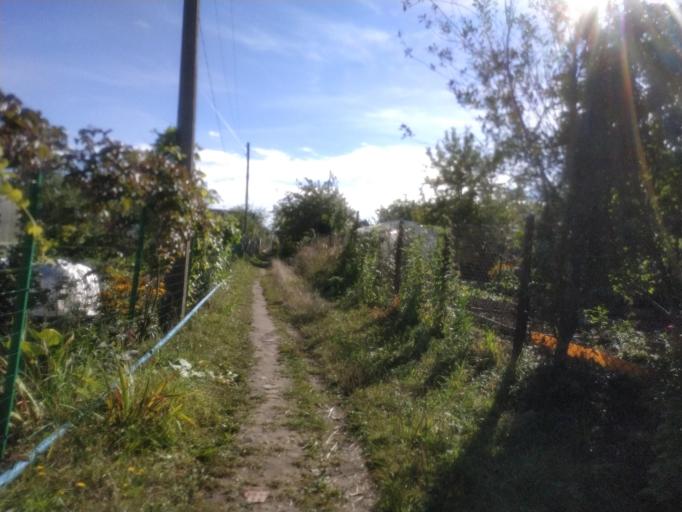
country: RU
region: Chuvashia
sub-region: Cheboksarskiy Rayon
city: Cheboksary
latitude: 56.1504
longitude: 47.1538
